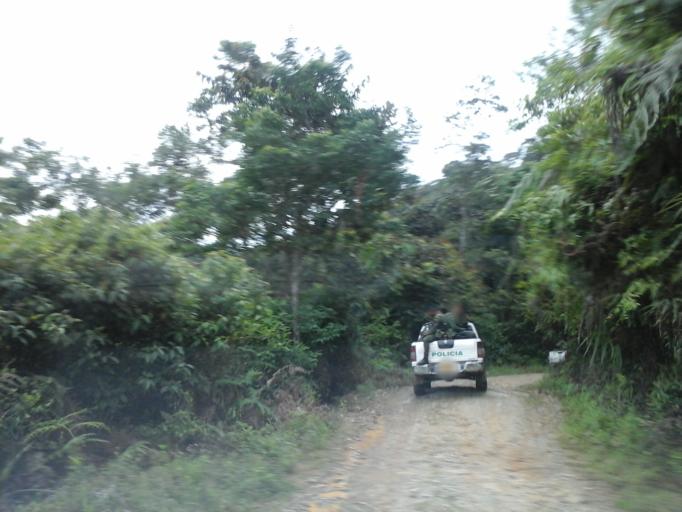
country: CO
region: Antioquia
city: San Roque
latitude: 6.5004
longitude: -74.9762
